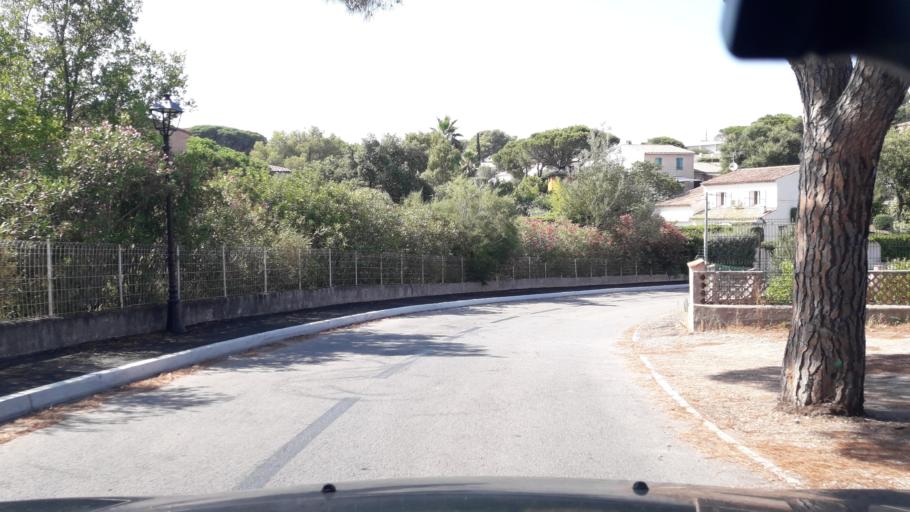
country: FR
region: Provence-Alpes-Cote d'Azur
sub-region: Departement du Var
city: Saint-Raphael
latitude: 43.4532
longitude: 6.7613
